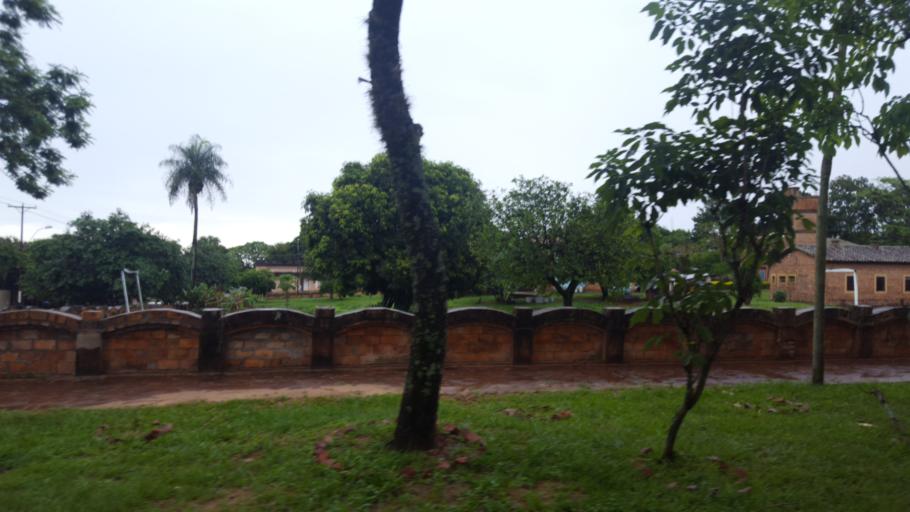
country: PY
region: Misiones
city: San Juan Bautista
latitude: -26.6706
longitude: -57.1473
